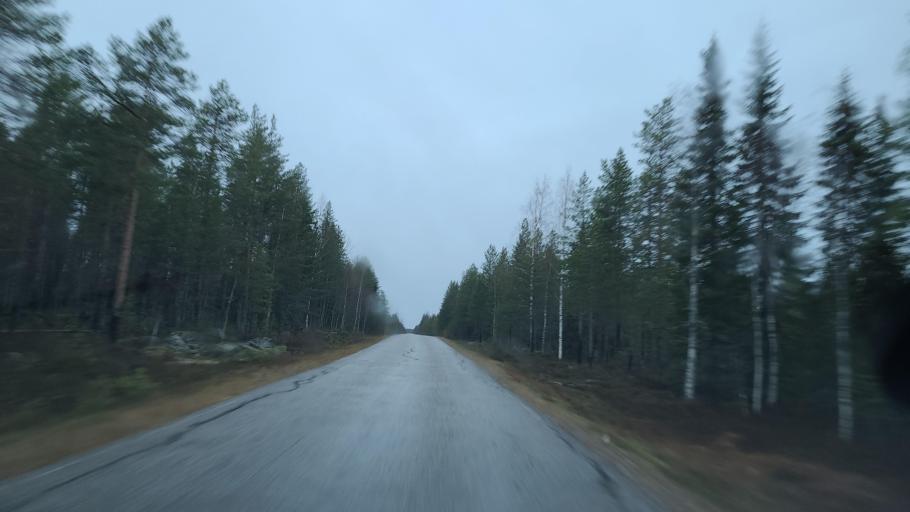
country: FI
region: Lapland
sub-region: Kemi-Tornio
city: Simo
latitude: 65.8869
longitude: 25.2200
